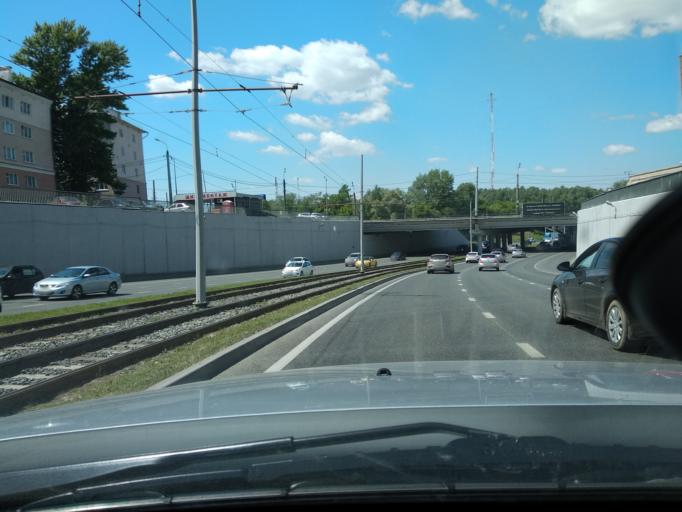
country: RU
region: Tatarstan
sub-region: Gorod Kazan'
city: Kazan
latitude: 55.8153
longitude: 49.1824
